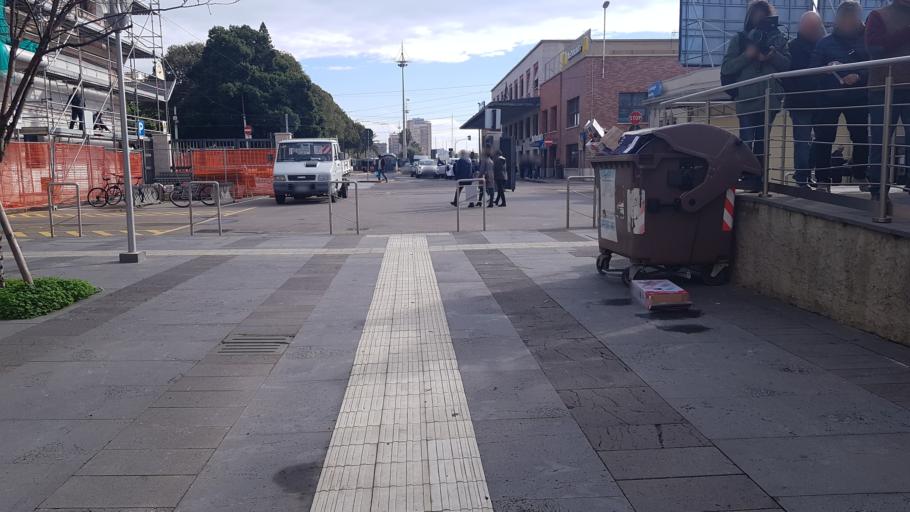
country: IT
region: Sardinia
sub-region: Provincia di Cagliari
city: Cagliari
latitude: 39.2155
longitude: 9.1084
